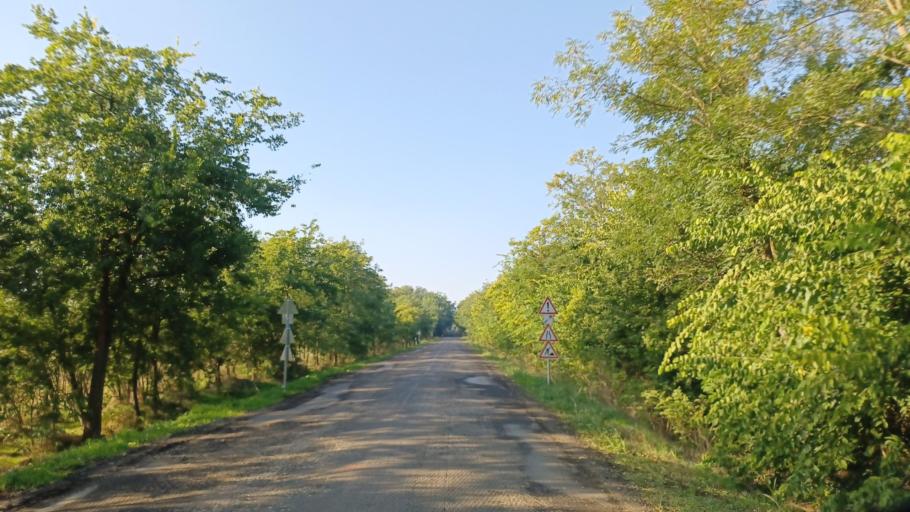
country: HU
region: Tolna
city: Szedres
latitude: 46.5281
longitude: 18.6451
